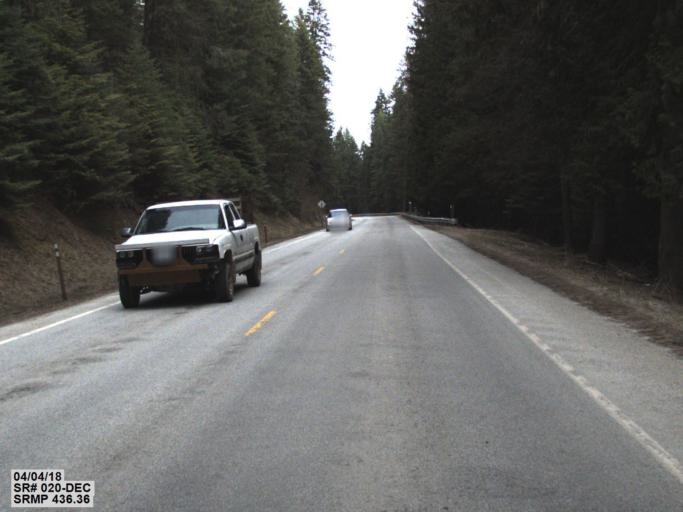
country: US
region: Washington
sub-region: Pend Oreille County
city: Newport
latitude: 48.1897
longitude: -117.0504
